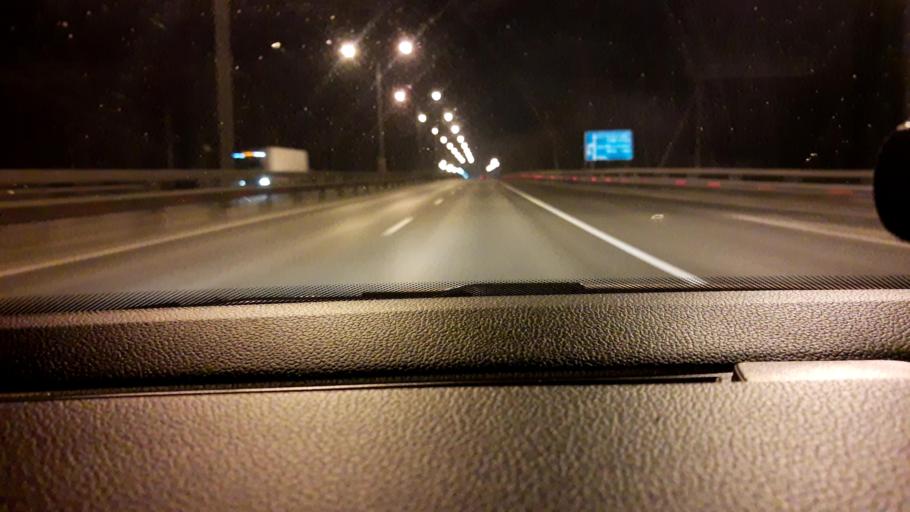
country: RU
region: Moskovskaya
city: Malaya Dubna
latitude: 55.8604
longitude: 38.8949
